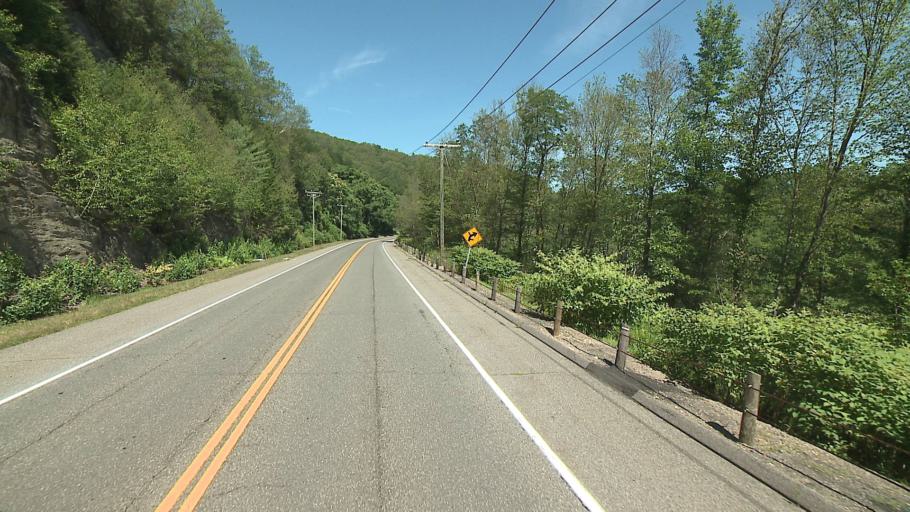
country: US
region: Connecticut
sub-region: Hartford County
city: Collinsville
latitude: 41.8005
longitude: -72.9279
